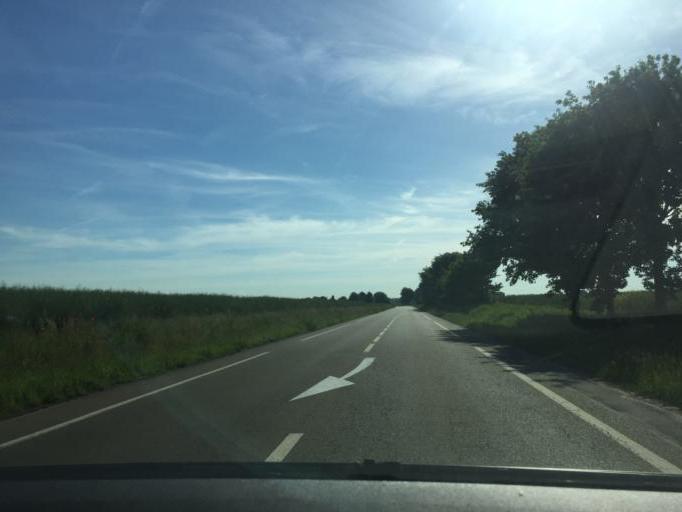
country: FR
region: Ile-de-France
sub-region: Departement de l'Essonne
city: Villiers-le-Bacle
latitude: 48.7406
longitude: 2.1126
